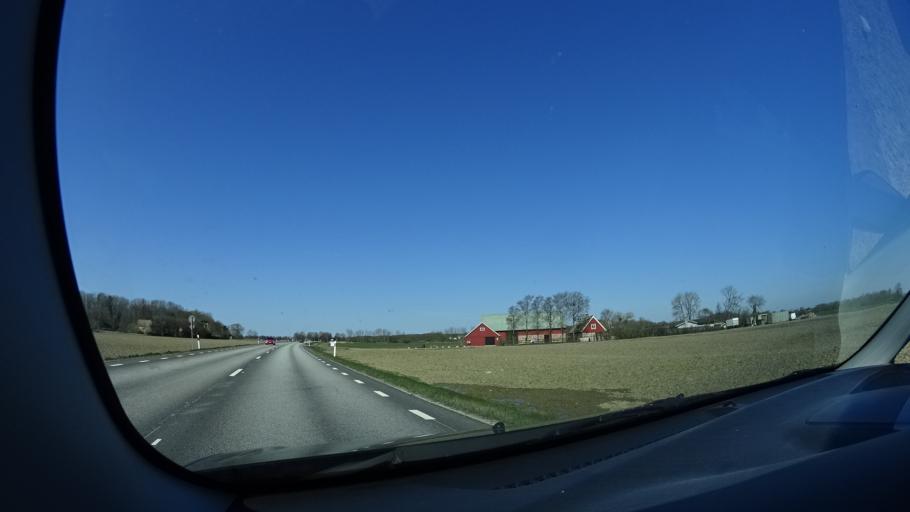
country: SE
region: Skane
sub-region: Angelholms Kommun
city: Strovelstorp
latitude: 56.2066
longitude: 12.7265
